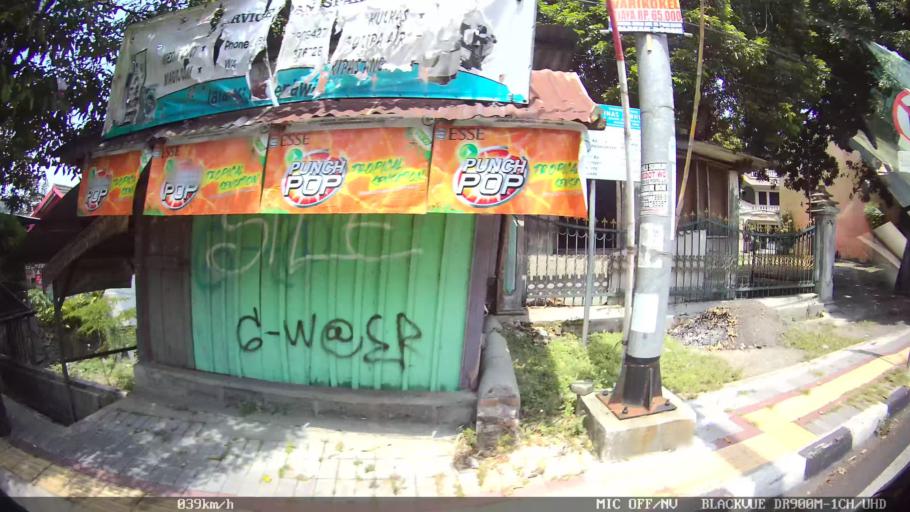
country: ID
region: Daerah Istimewa Yogyakarta
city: Yogyakarta
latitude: -7.8143
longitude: 110.3923
